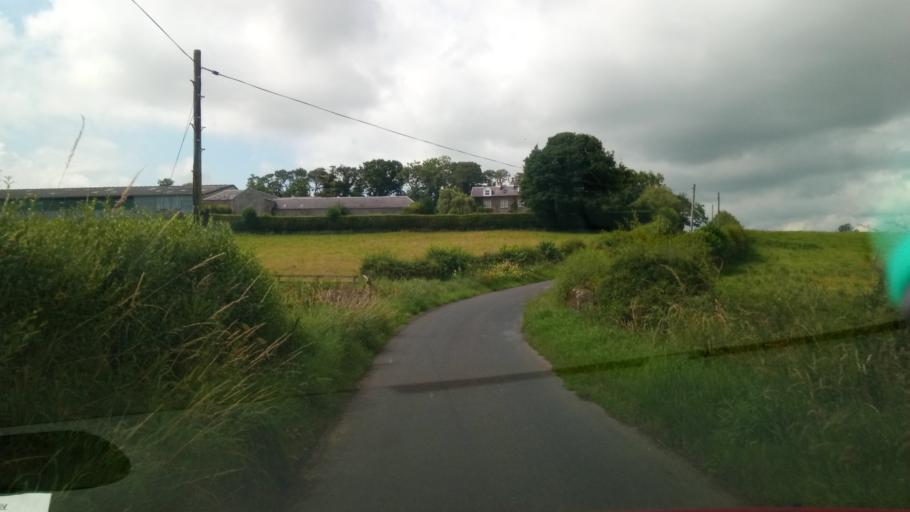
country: GB
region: Scotland
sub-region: The Scottish Borders
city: Hawick
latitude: 55.4403
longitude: -2.7009
